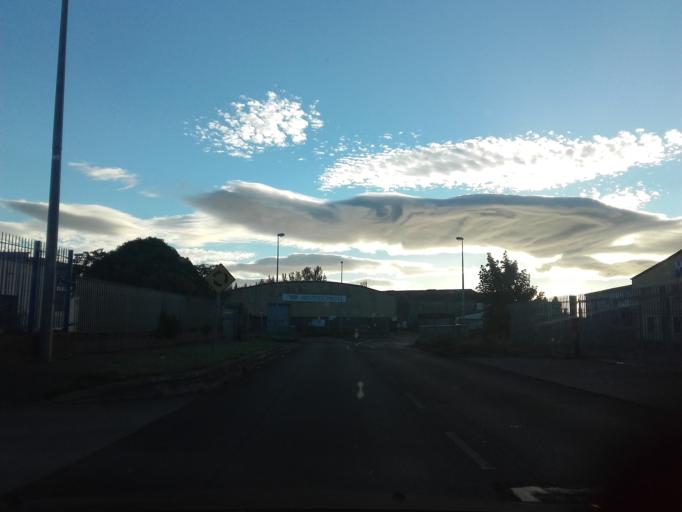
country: IE
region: Leinster
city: Tallaght
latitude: 53.2948
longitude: -6.3777
